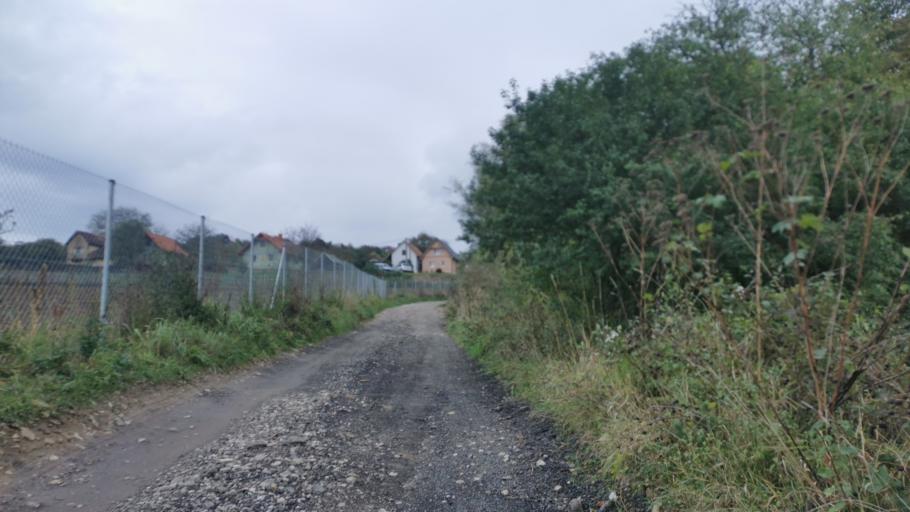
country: SK
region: Trnavsky
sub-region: Okres Skalica
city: Skalica
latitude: 48.8172
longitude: 17.2175
